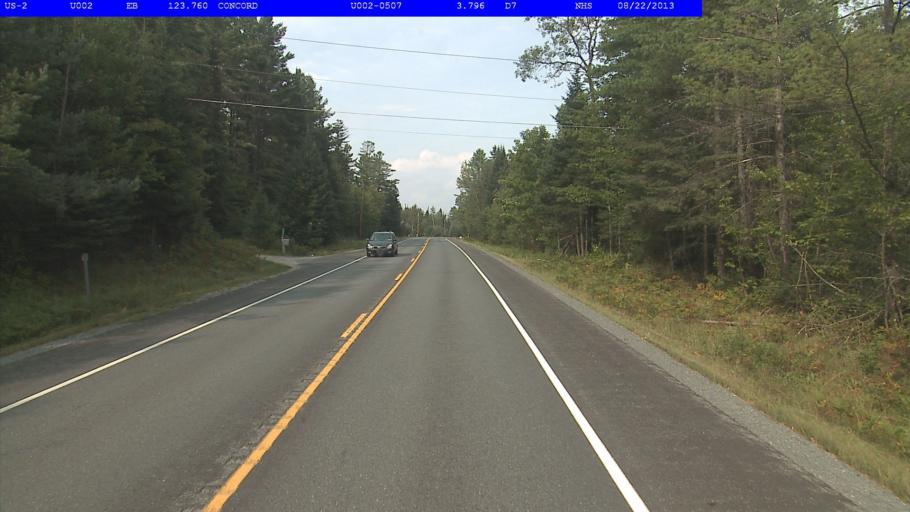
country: US
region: Vermont
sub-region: Caledonia County
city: St Johnsbury
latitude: 44.4483
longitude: -71.8739
